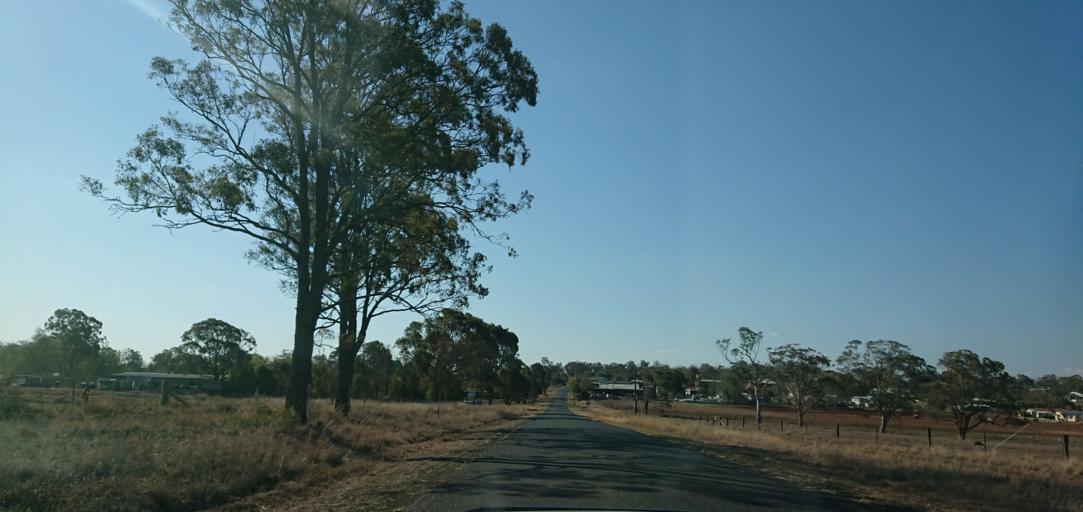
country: AU
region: Queensland
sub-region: Toowoomba
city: Westbrook
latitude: -27.6838
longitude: 151.7136
